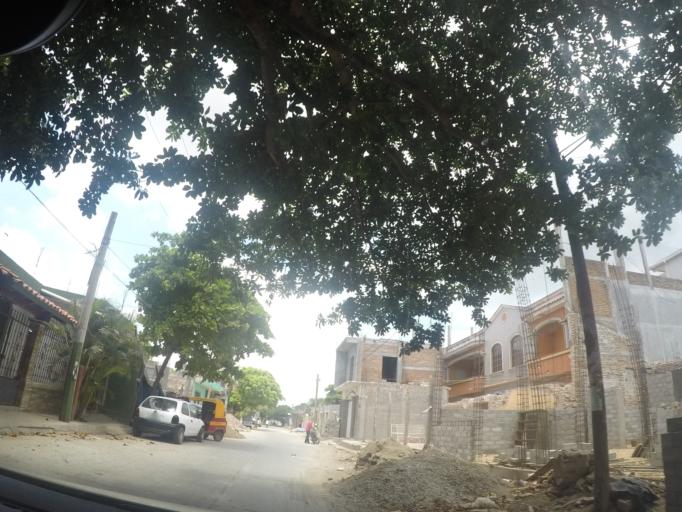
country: MX
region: Oaxaca
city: Juchitan de Zaragoza
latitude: 16.4280
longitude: -95.0216
